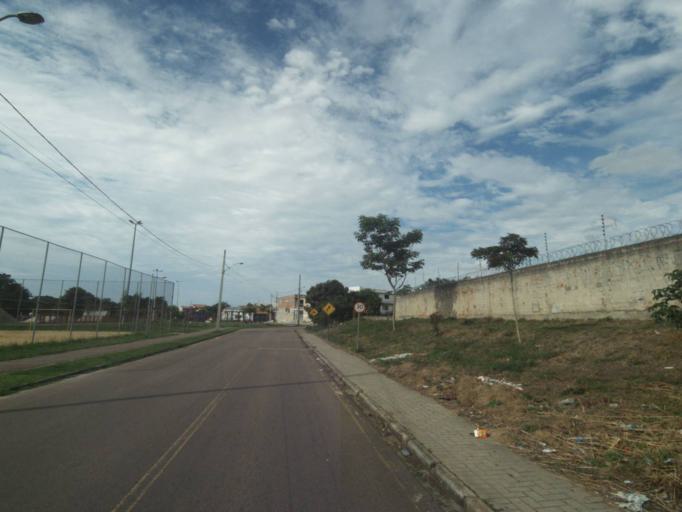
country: BR
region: Parana
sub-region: Curitiba
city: Curitiba
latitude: -25.5079
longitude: -49.3363
